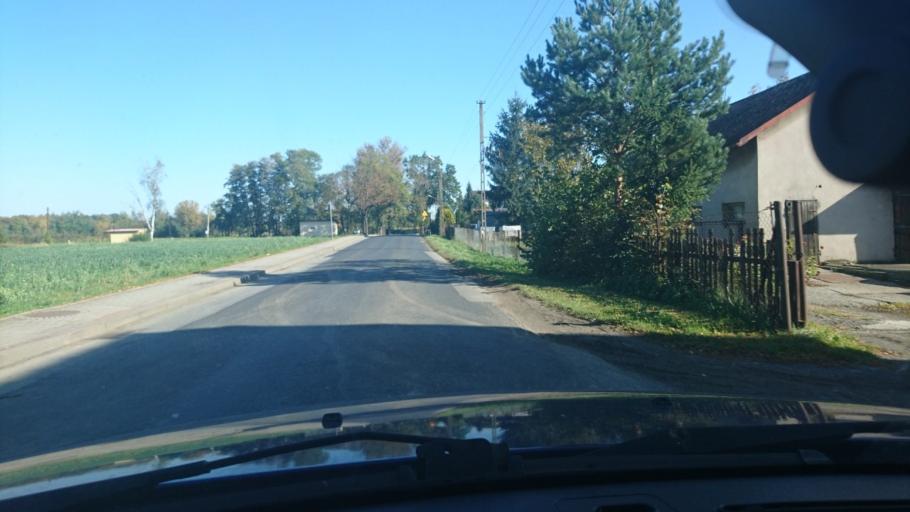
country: PL
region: Silesian Voivodeship
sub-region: Powiat bielski
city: Bronow
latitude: 49.8519
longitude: 18.9419
